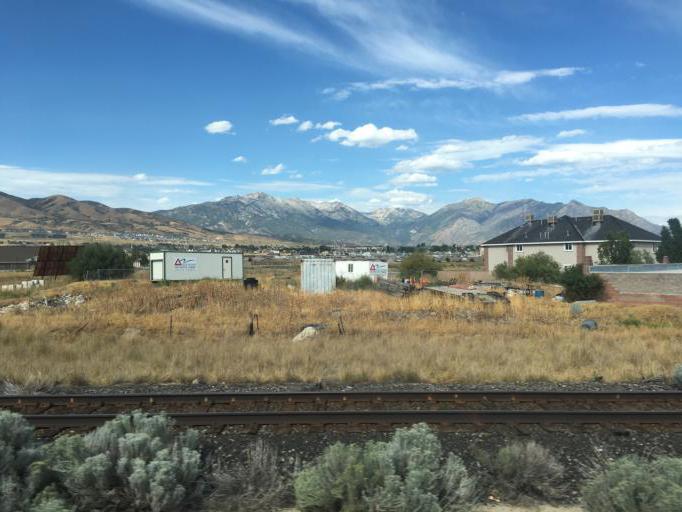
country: US
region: Utah
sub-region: Utah County
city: Lehi
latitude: 40.4115
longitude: -111.8807
